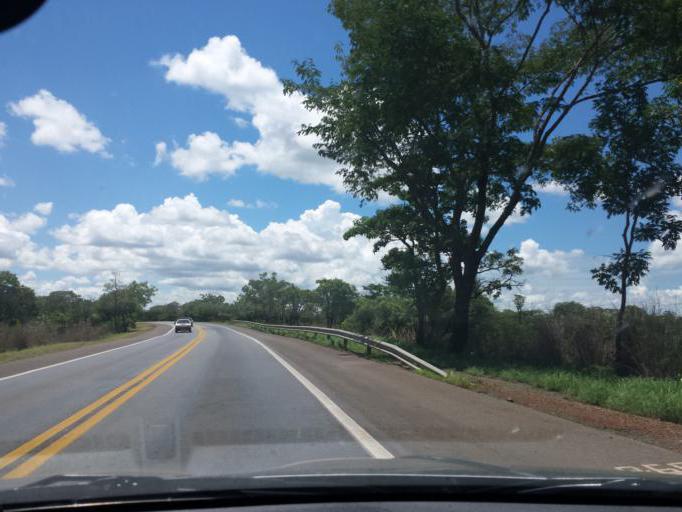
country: BR
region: Goias
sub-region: Cristalina
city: Cristalina
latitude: -16.6463
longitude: -47.7392
